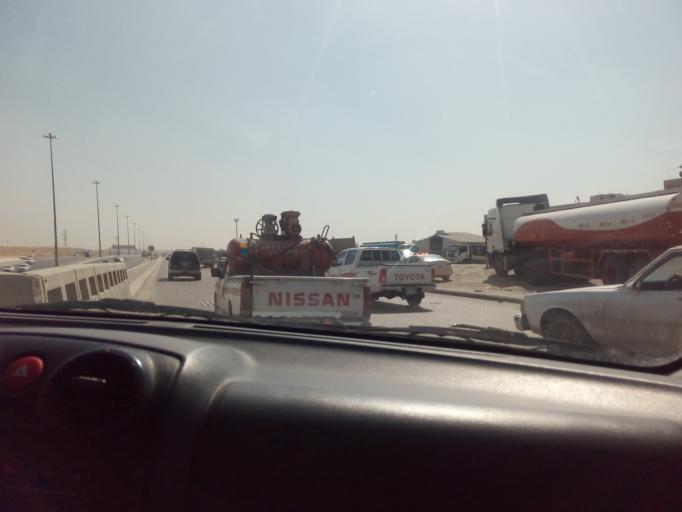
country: SA
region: Ar Riyad
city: Riyadh
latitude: 24.6782
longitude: 46.8565
